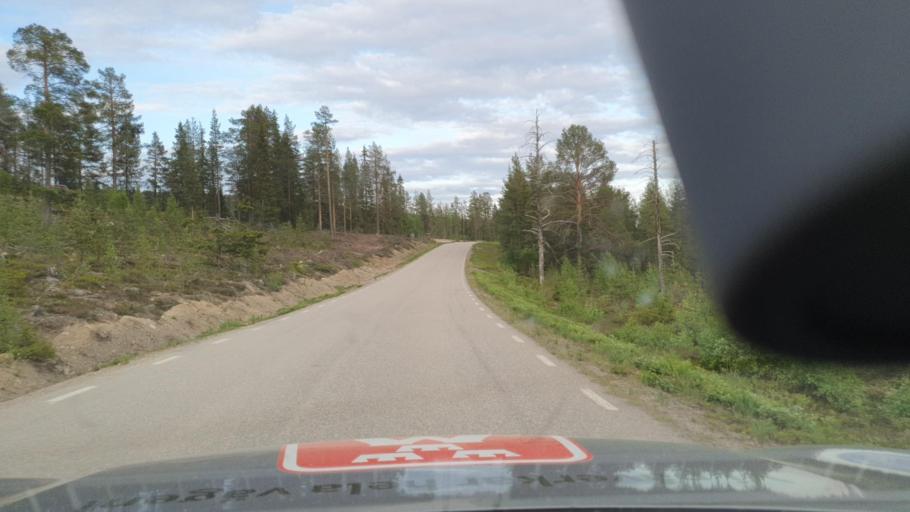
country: SE
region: Norrbotten
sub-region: Gallivare Kommun
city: Gaellivare
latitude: 66.7562
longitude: 21.0546
